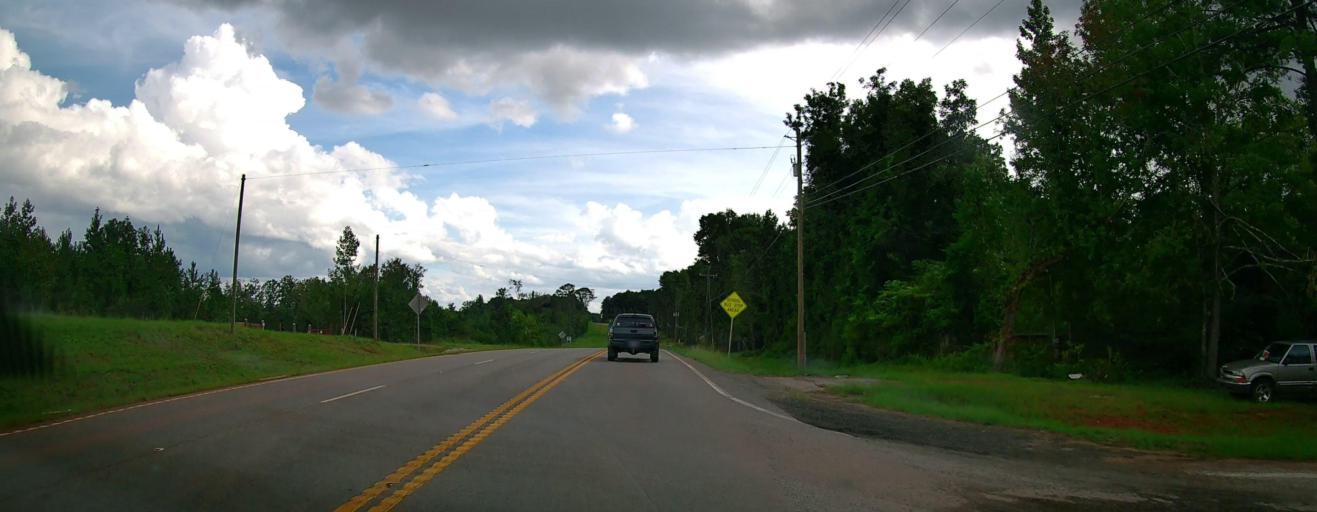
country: US
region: Georgia
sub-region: Harris County
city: Hamilton
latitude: 32.7240
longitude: -84.8741
